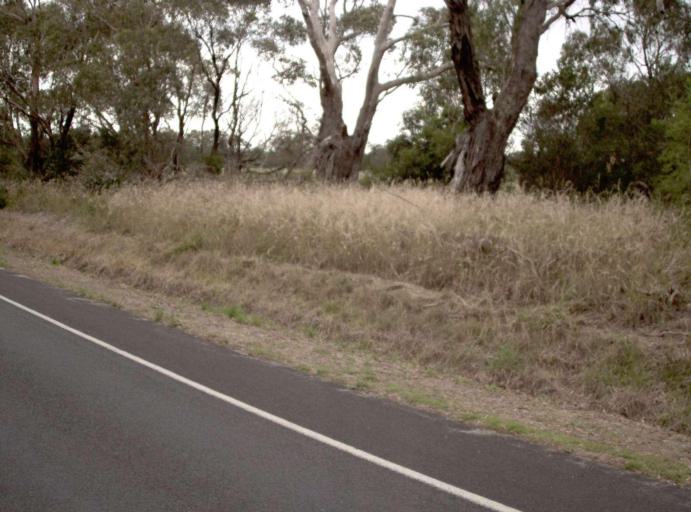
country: AU
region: Victoria
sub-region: Wellington
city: Sale
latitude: -38.1789
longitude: 147.0850
